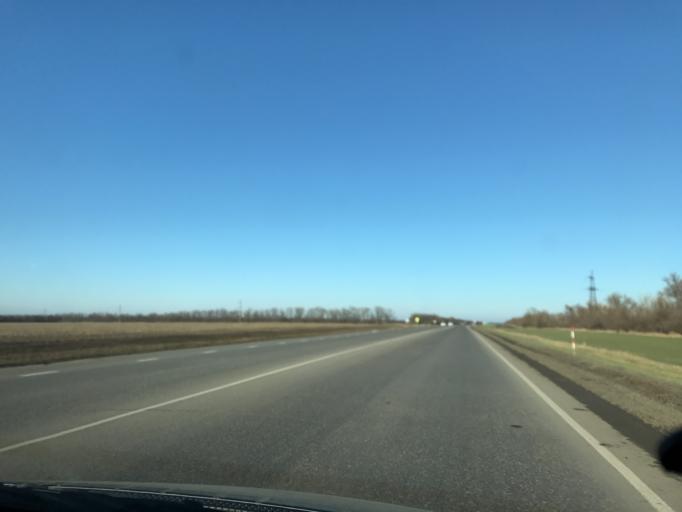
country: RU
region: Rostov
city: Kagal'nitskaya
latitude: 46.9260
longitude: 40.1001
